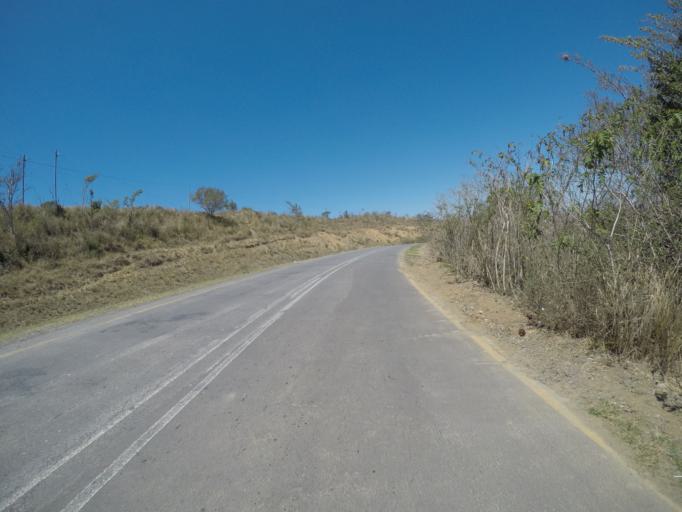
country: ZA
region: Eastern Cape
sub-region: OR Tambo District Municipality
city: Mthatha
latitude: -31.9114
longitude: 28.9607
